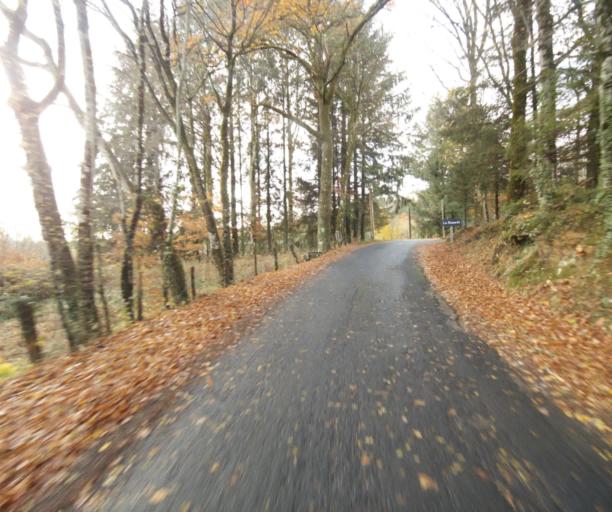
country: FR
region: Limousin
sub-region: Departement de la Correze
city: Cornil
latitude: 45.2222
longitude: 1.6894
